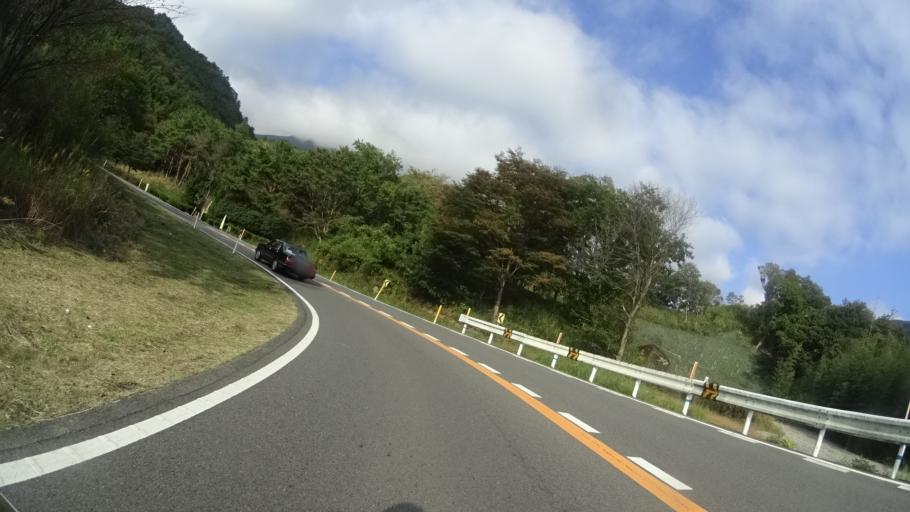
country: JP
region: Oita
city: Beppu
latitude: 33.2624
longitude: 131.3762
